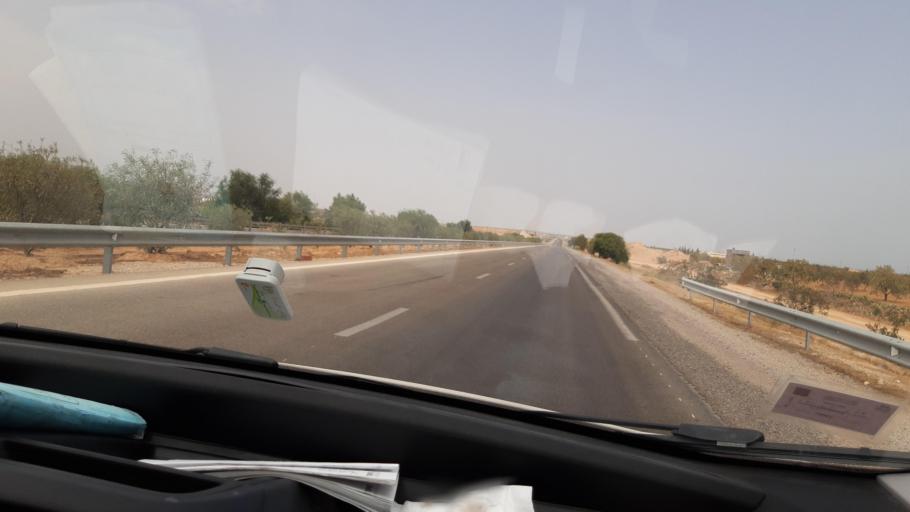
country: TN
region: Safaqis
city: Sfax
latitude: 34.8781
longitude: 10.7007
